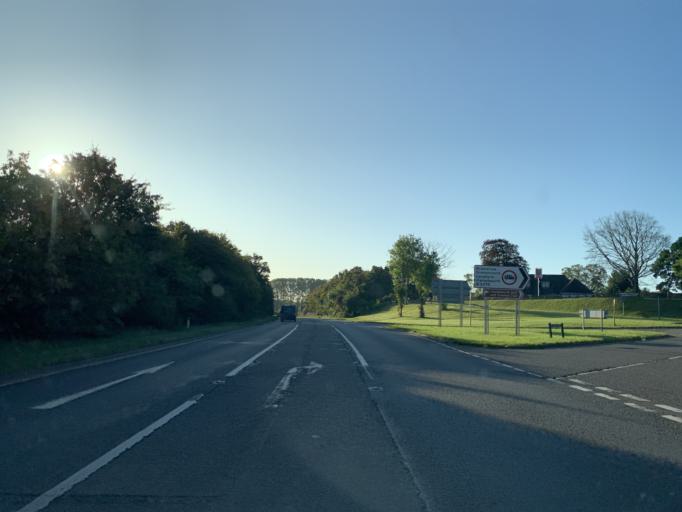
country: GB
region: England
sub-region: Wiltshire
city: Whiteparish
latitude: 50.9816
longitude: -1.6375
